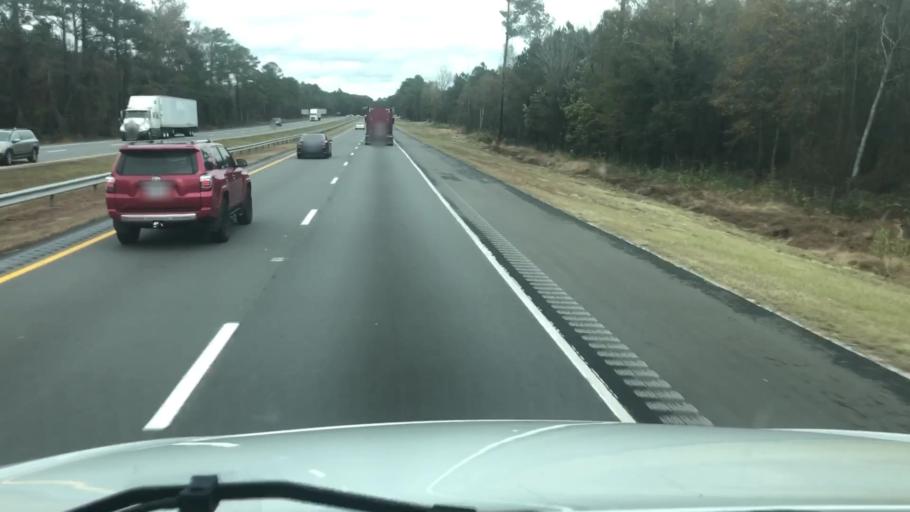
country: US
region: North Carolina
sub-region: Cumberland County
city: Eastover
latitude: 35.1052
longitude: -78.7708
